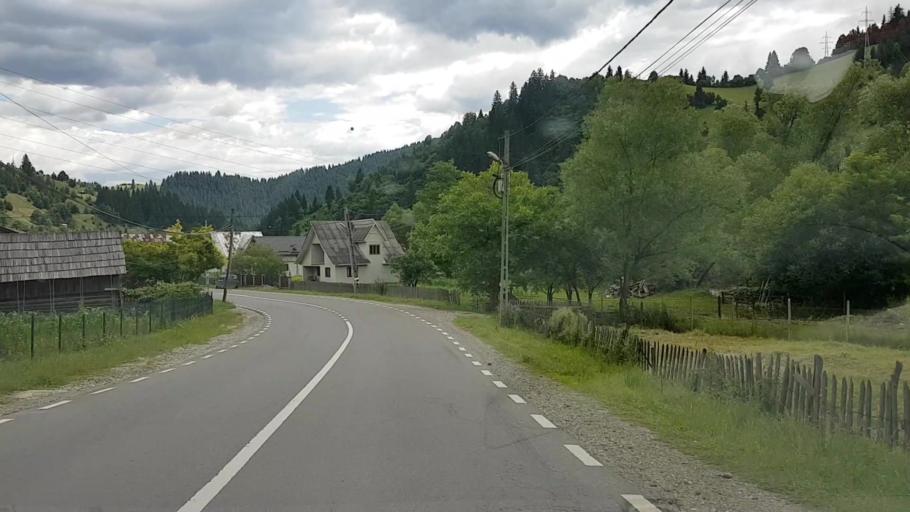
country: RO
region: Neamt
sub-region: Comuna Farcasa
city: Farcasa
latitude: 47.1582
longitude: 25.8317
